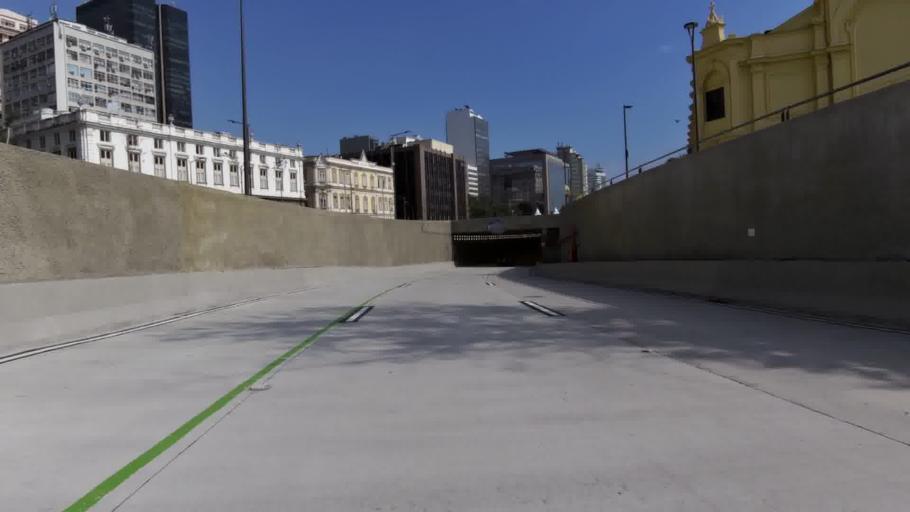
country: BR
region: Rio de Janeiro
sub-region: Rio De Janeiro
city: Rio de Janeiro
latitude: -22.9042
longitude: -43.1717
